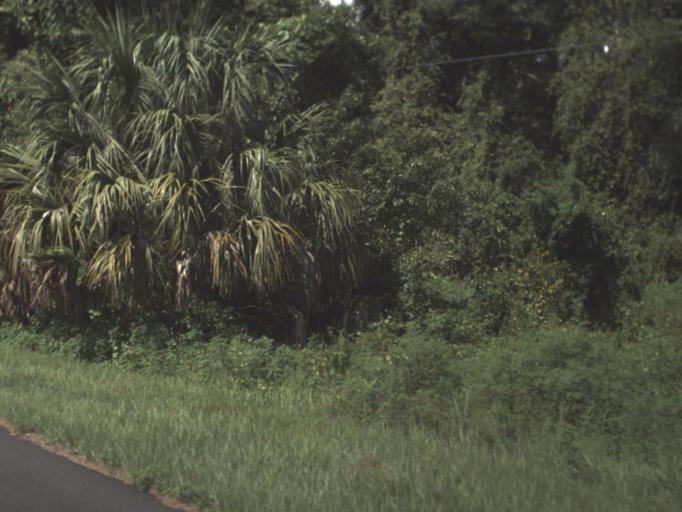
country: US
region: Florida
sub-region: Citrus County
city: Floral City
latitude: 28.7459
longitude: -82.2986
